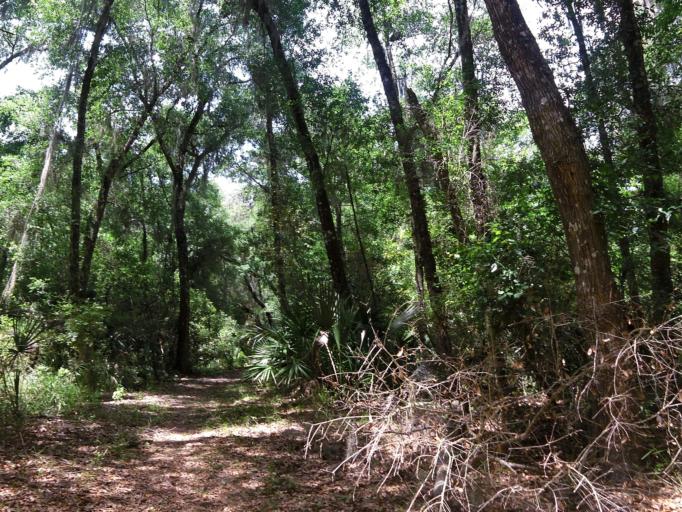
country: US
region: Florida
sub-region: Nassau County
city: Fernandina Beach
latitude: 30.4937
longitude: -81.4882
